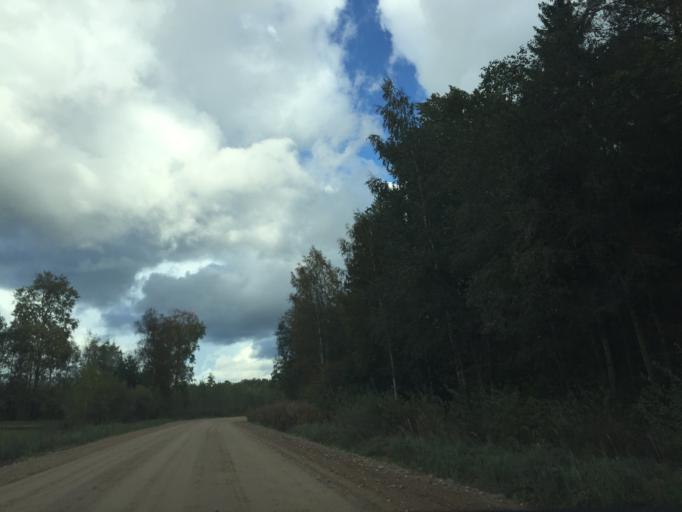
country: LV
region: Malpils
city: Malpils
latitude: 57.0573
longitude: 25.1325
